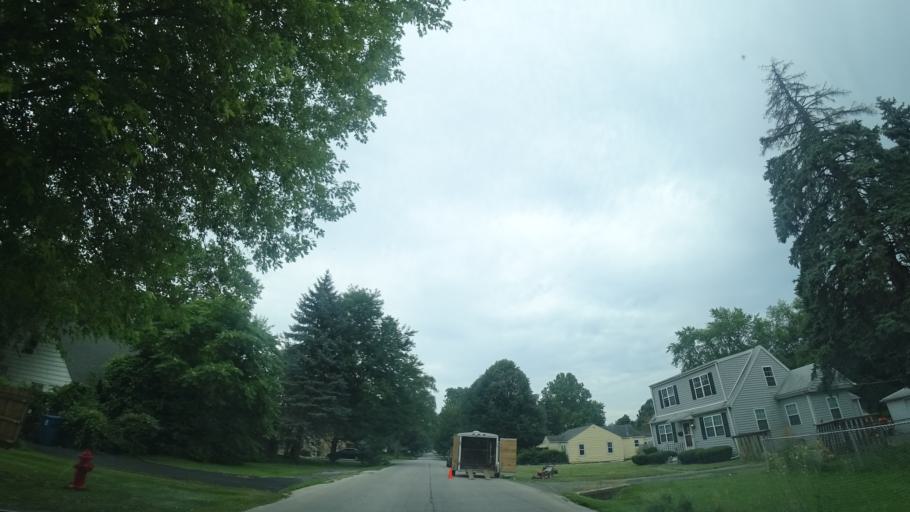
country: US
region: Illinois
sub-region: Cook County
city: Merrionette Park
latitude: 41.6802
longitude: -87.7174
